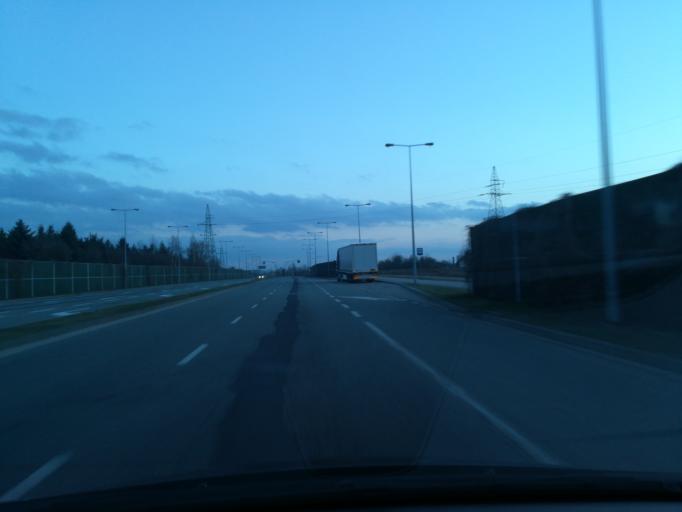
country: PL
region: Lodz Voivodeship
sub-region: Piotrkow Trybunalski
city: Piotrkow Trybunalski
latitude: 51.4104
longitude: 19.6562
